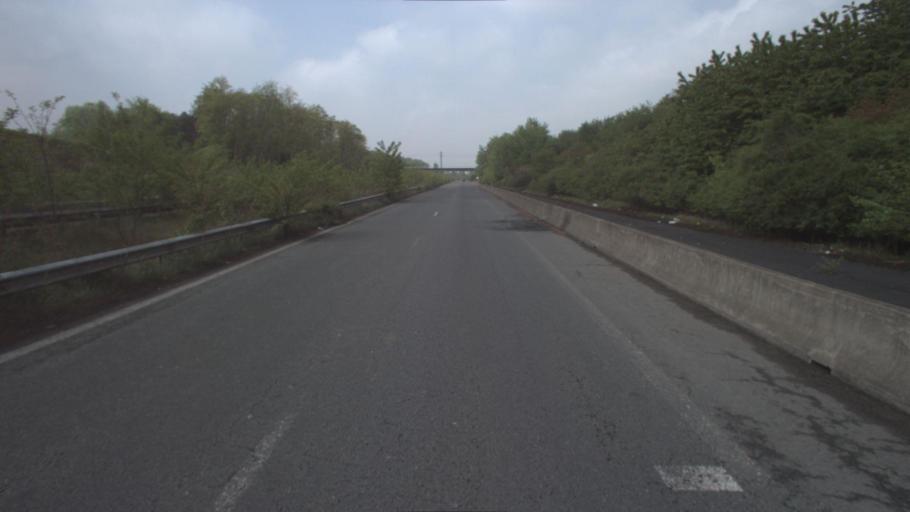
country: FR
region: Ile-de-France
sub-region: Departement de Seine-Saint-Denis
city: Villepinte
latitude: 48.9566
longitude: 2.5217
